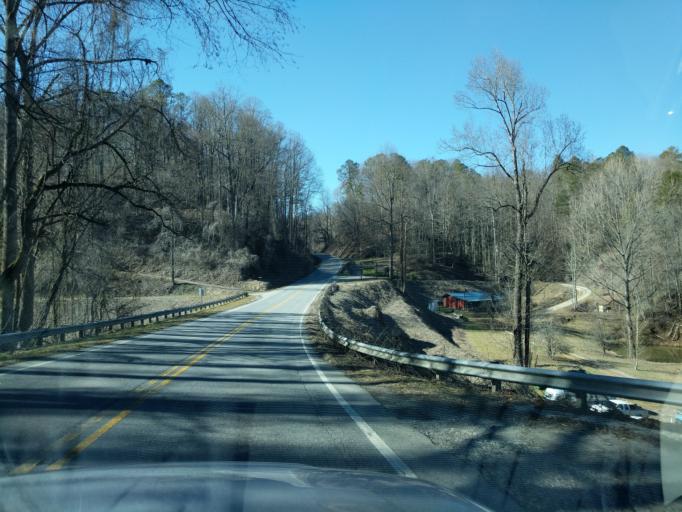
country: US
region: North Carolina
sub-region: Swain County
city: Bryson City
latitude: 35.3373
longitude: -83.5655
